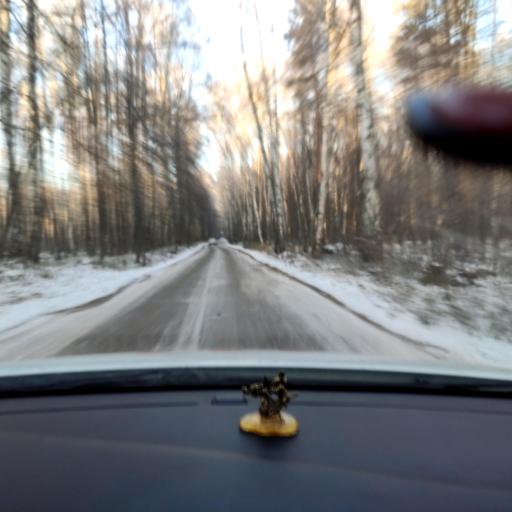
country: RU
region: Tatarstan
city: Stolbishchi
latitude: 55.6744
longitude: 49.1041
